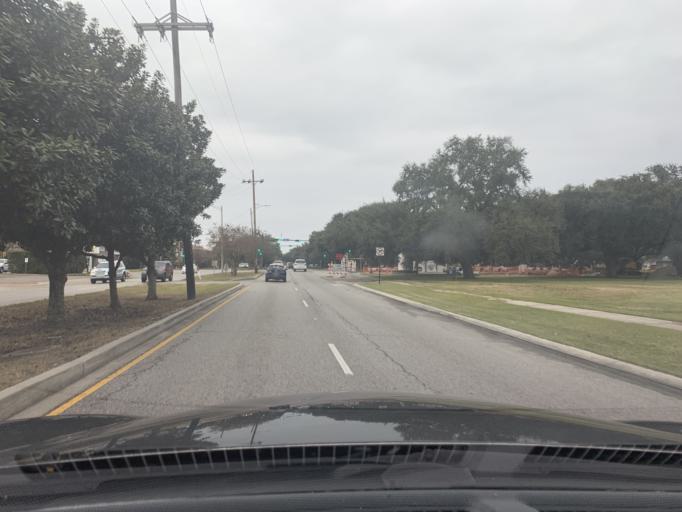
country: US
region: Louisiana
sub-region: Jefferson Parish
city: Metairie
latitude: 30.0195
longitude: -90.1052
